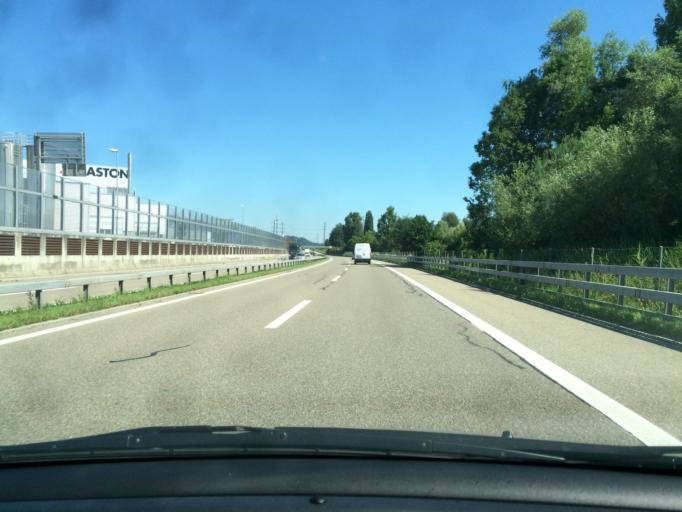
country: CH
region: Saint Gallen
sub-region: Wahlkreis Rheintal
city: Diepoldsau
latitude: 47.4045
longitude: 9.6484
